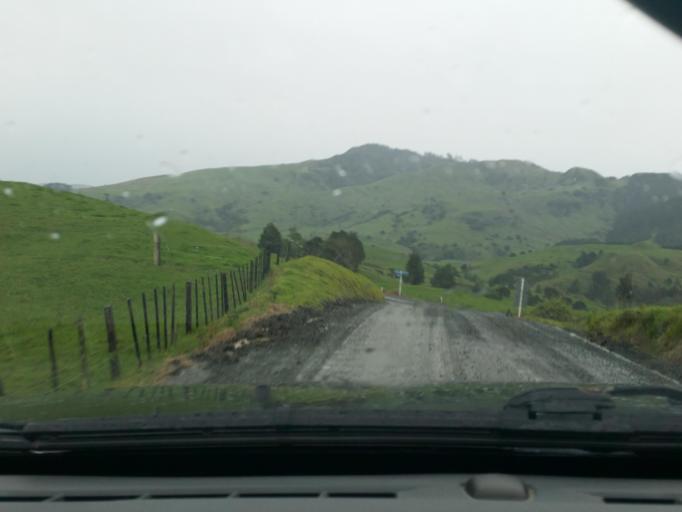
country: NZ
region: Northland
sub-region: Kaipara District
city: Dargaville
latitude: -35.8154
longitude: 173.8091
